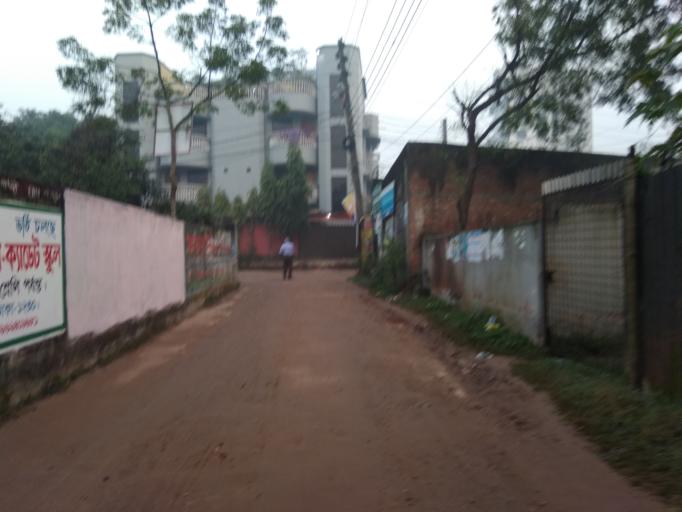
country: BD
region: Dhaka
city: Tungi
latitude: 23.8607
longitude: 90.4324
